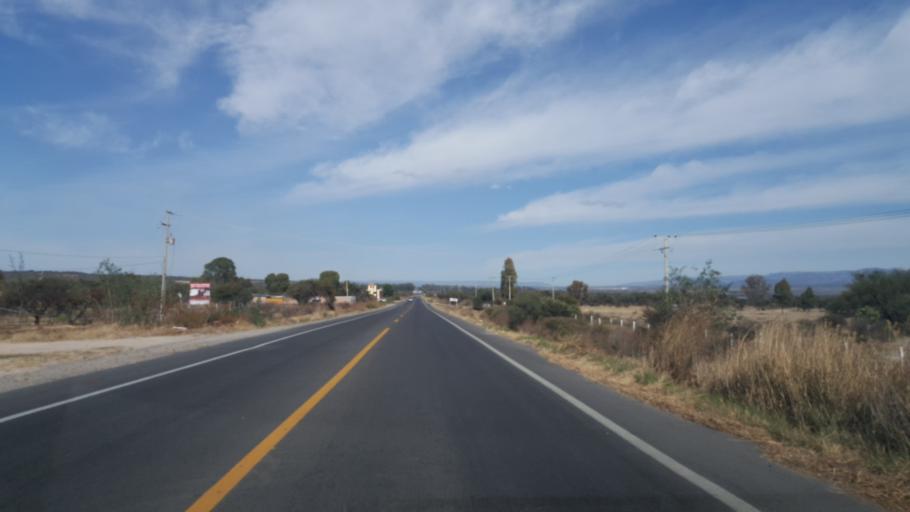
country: MX
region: Jalisco
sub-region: Lagos de Moreno
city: Cristeros [Fraccionamiento]
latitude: 21.2610
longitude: -101.9470
